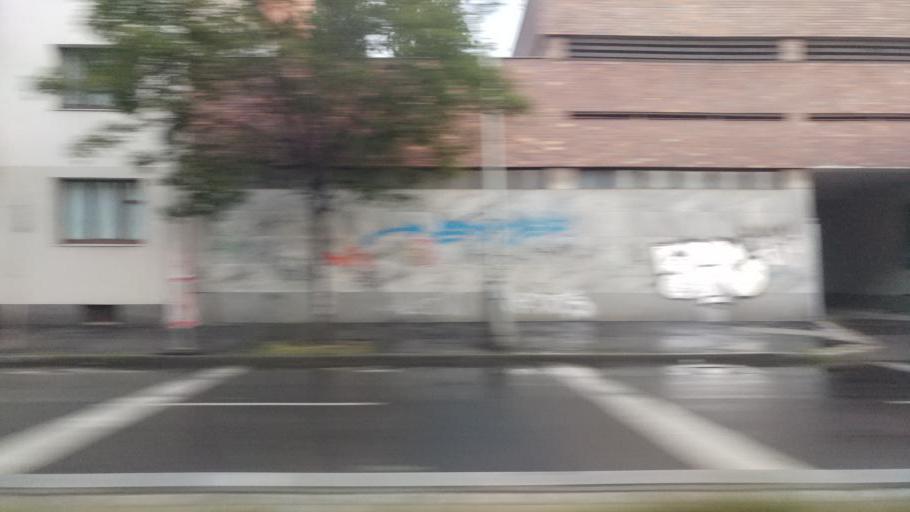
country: CZ
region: Praha
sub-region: Praha 8
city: Karlin
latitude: 50.0685
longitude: 14.4658
